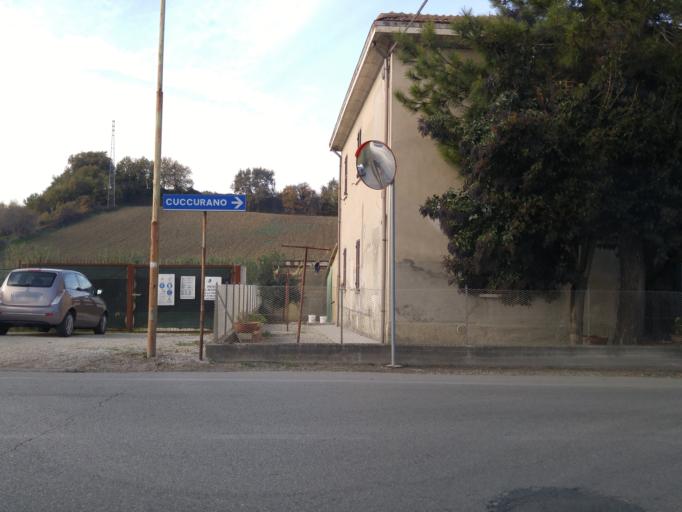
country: IT
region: The Marches
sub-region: Provincia di Pesaro e Urbino
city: Cuccurano
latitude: 43.7959
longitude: 12.9588
